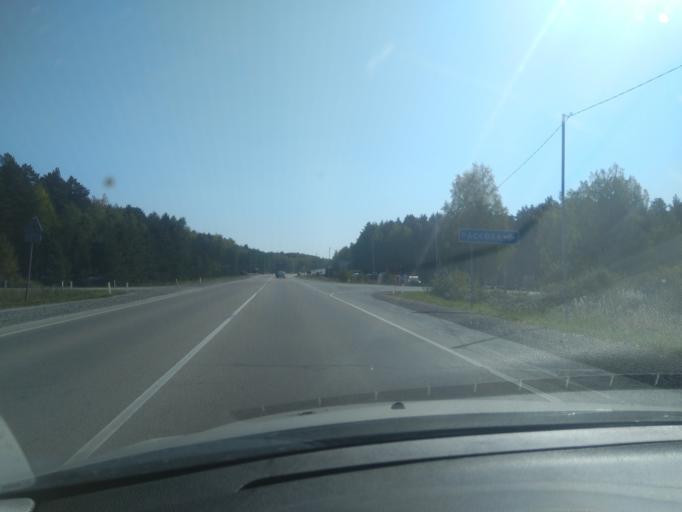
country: RU
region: Sverdlovsk
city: Verkhneye Dubrovo
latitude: 56.7231
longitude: 61.0455
